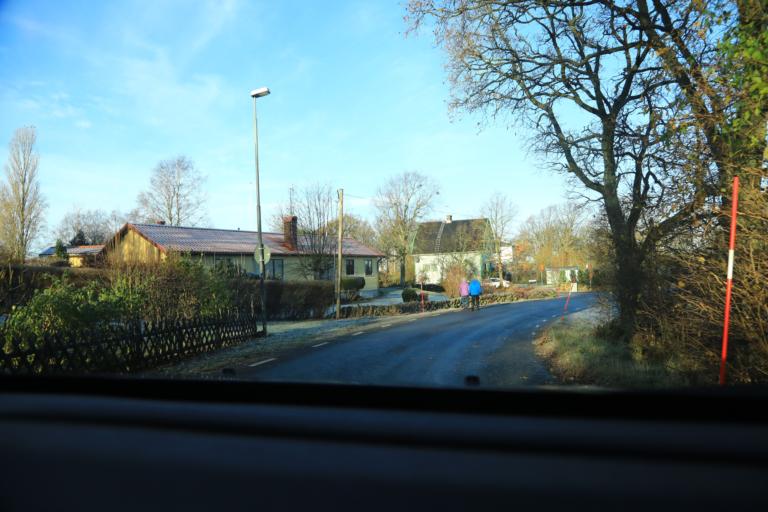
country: SE
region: Halland
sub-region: Varbergs Kommun
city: Varberg
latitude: 57.1934
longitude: 12.2174
